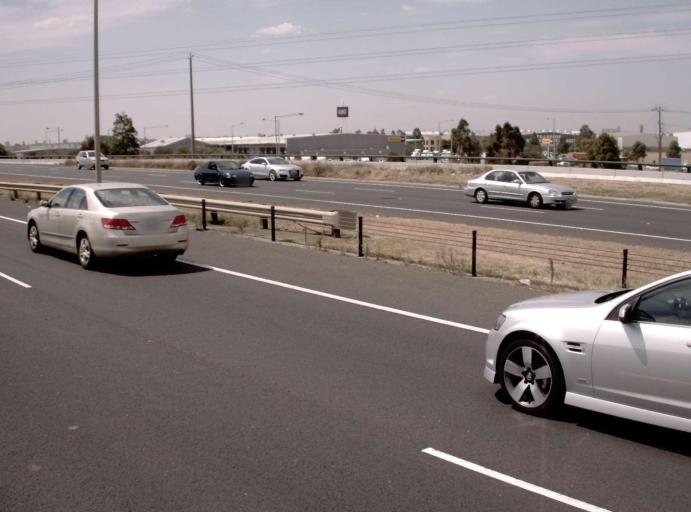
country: AU
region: Victoria
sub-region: Brimbank
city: Sunshine West
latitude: -37.8166
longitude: 144.8083
